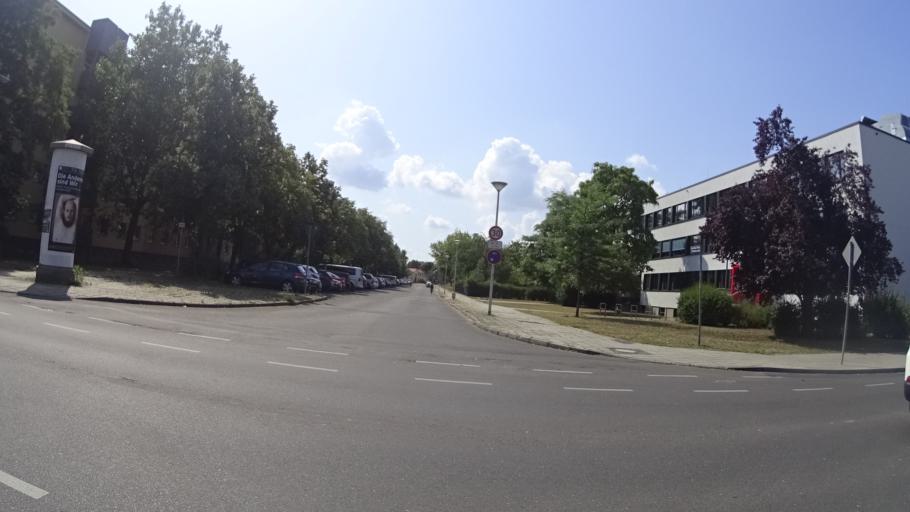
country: DE
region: Brandenburg
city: Cottbus
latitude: 51.7661
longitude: 14.3251
